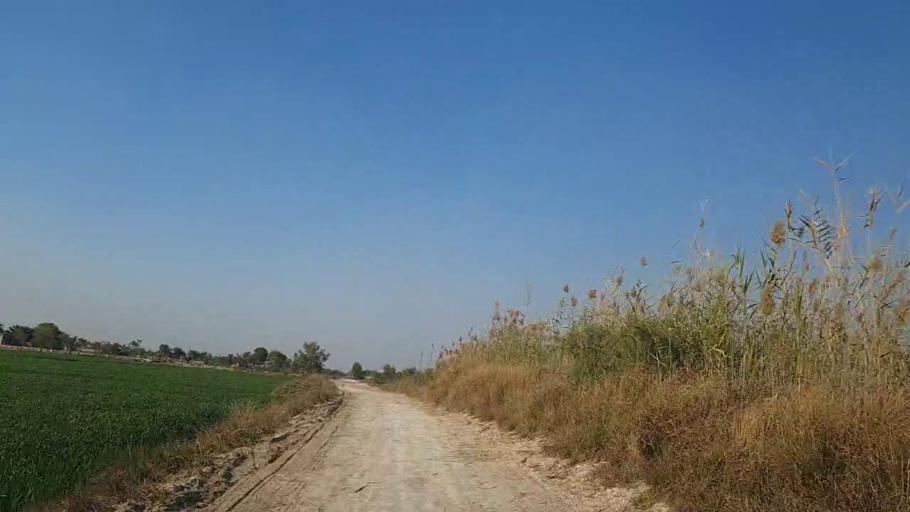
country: PK
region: Sindh
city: Daur
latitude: 26.3279
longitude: 68.1772
